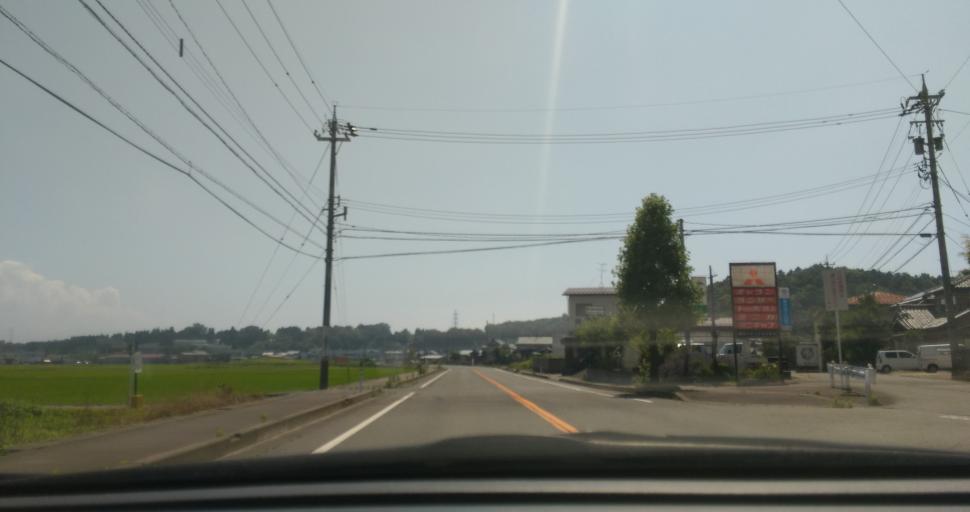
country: JP
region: Fukui
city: Mikuni
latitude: 36.2246
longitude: 136.1635
